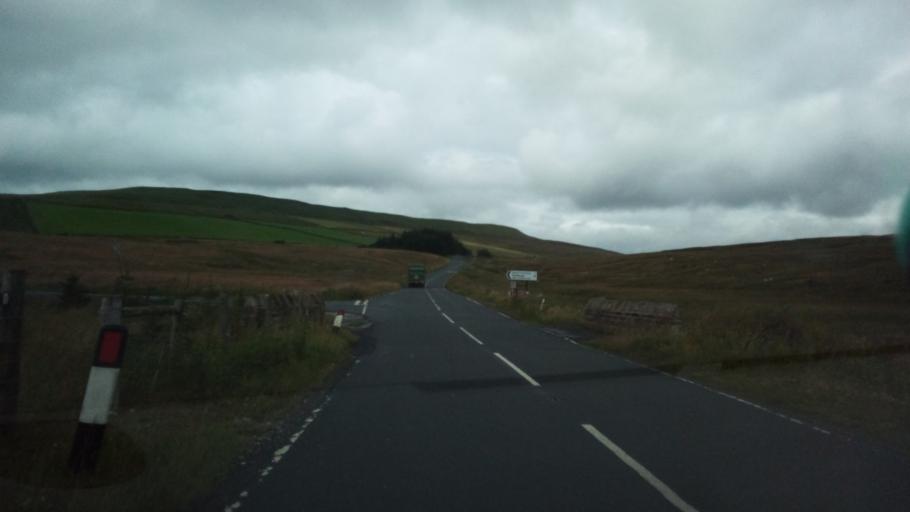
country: GB
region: England
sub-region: North Yorkshire
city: Ingleton
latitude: 54.2472
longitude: -2.3161
